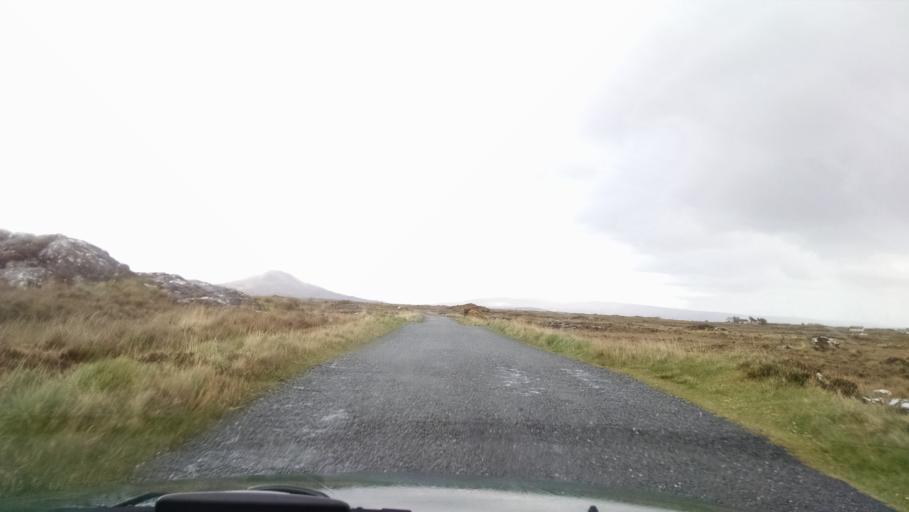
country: IE
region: Connaught
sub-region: County Galway
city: Clifden
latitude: 53.4352
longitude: -9.9076
